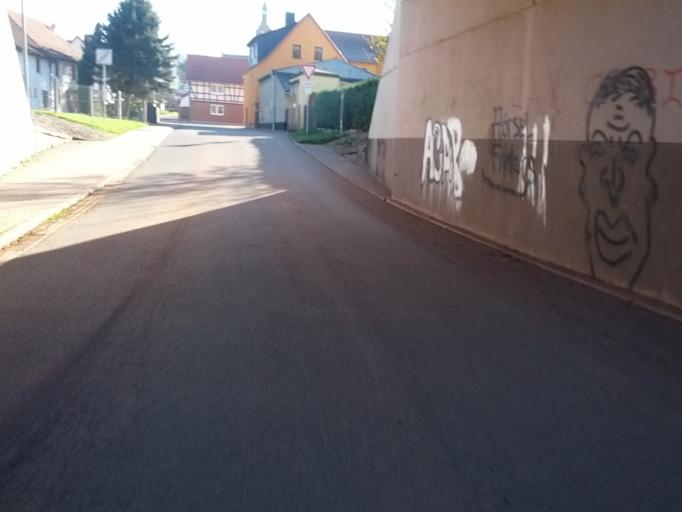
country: DE
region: Thuringia
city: Seebach
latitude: 50.9435
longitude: 10.4597
